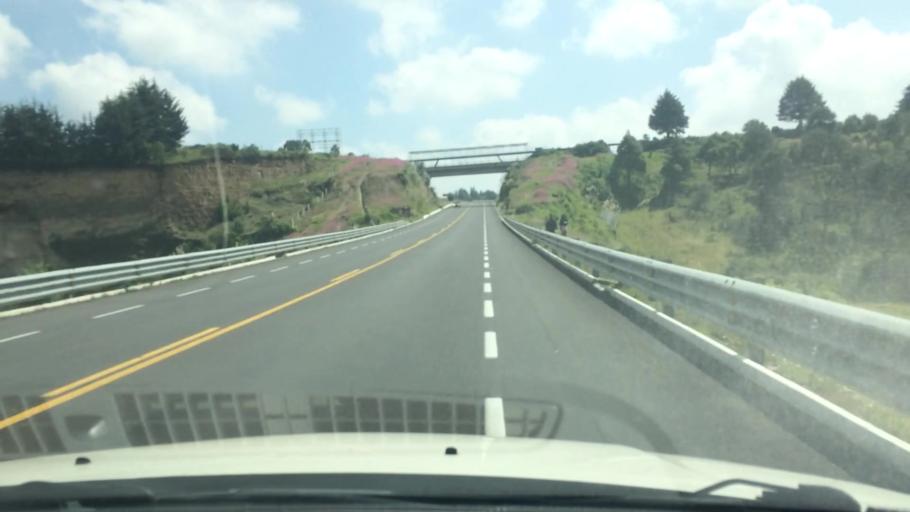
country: MX
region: Mexico
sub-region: Villa Victoria
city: Colonia Doctor Gustavo Baz
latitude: 19.3769
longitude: -99.8857
